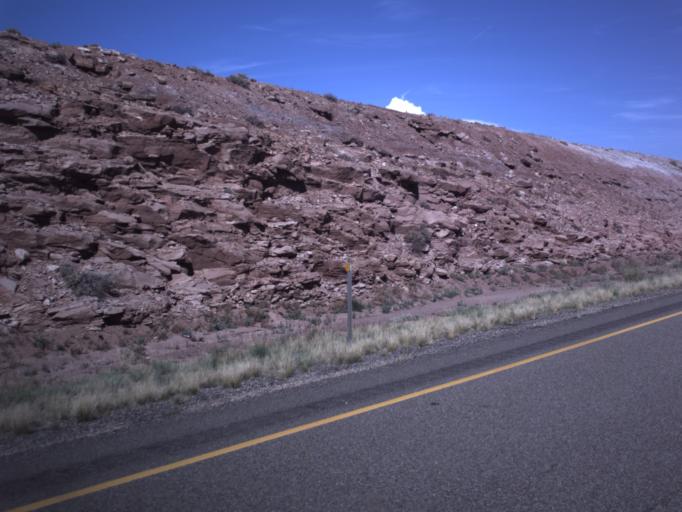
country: US
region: Utah
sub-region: Carbon County
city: East Carbon City
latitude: 38.9211
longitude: -110.3867
